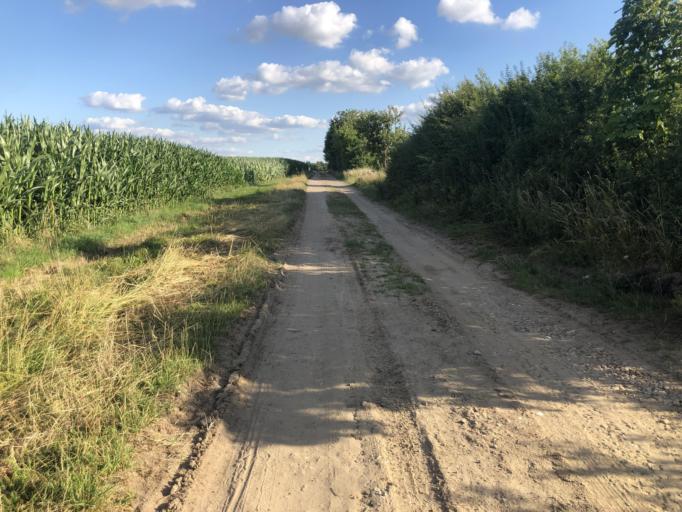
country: DE
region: Lower Saxony
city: Tosterglope
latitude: 53.2565
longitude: 10.7832
